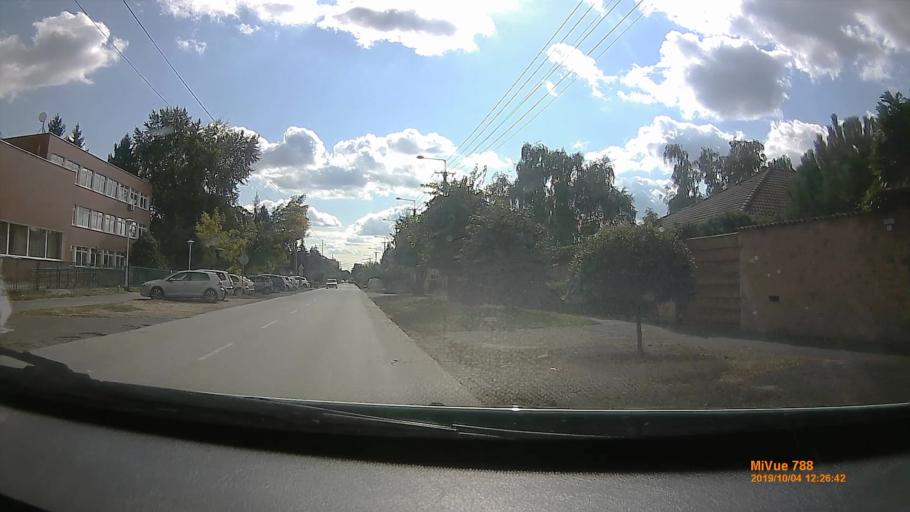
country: HU
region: Szabolcs-Szatmar-Bereg
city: Nyiregyhaza
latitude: 47.9754
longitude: 21.7063
